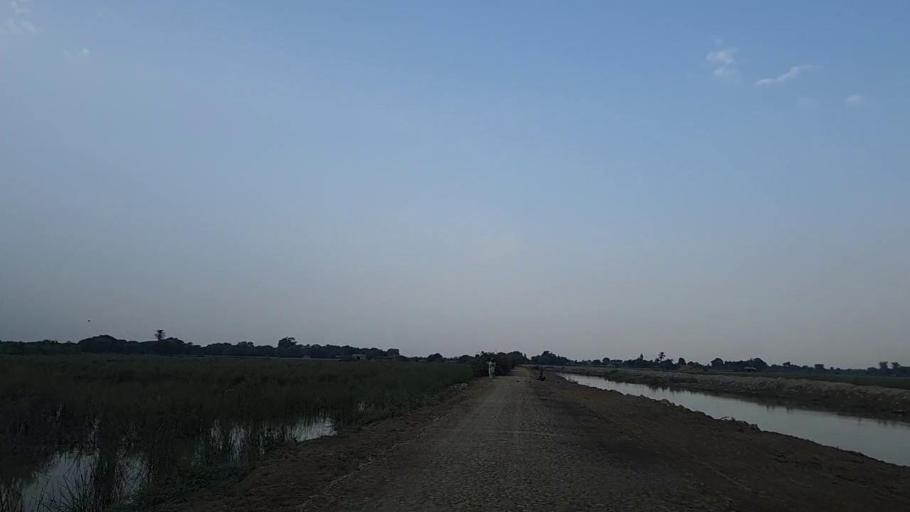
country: PK
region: Sindh
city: Daro Mehar
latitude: 24.7606
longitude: 68.1359
